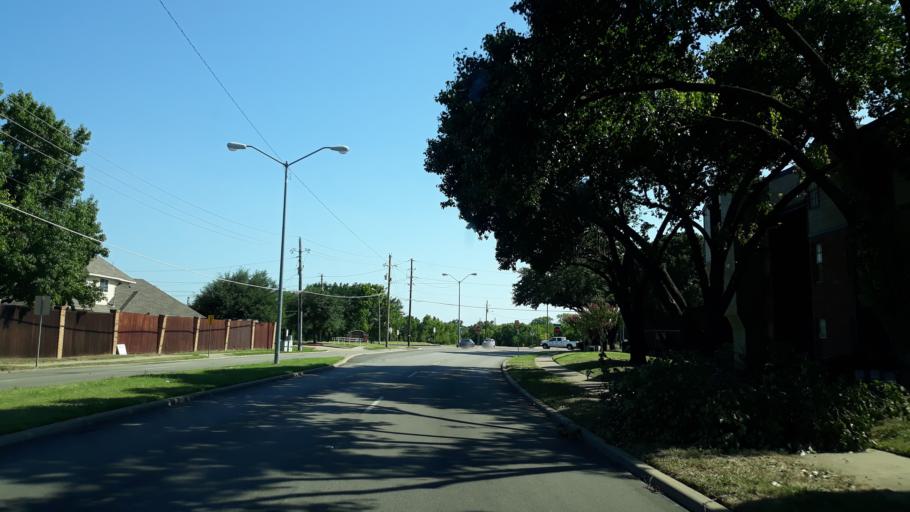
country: US
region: Texas
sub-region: Dallas County
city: Irving
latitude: 32.8248
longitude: -97.0105
